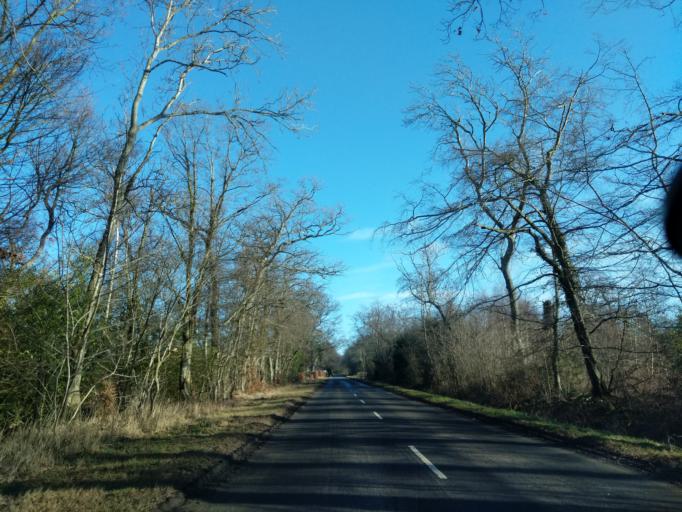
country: GB
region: Scotland
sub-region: East Lothian
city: Haddington
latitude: 55.9582
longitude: -2.7347
